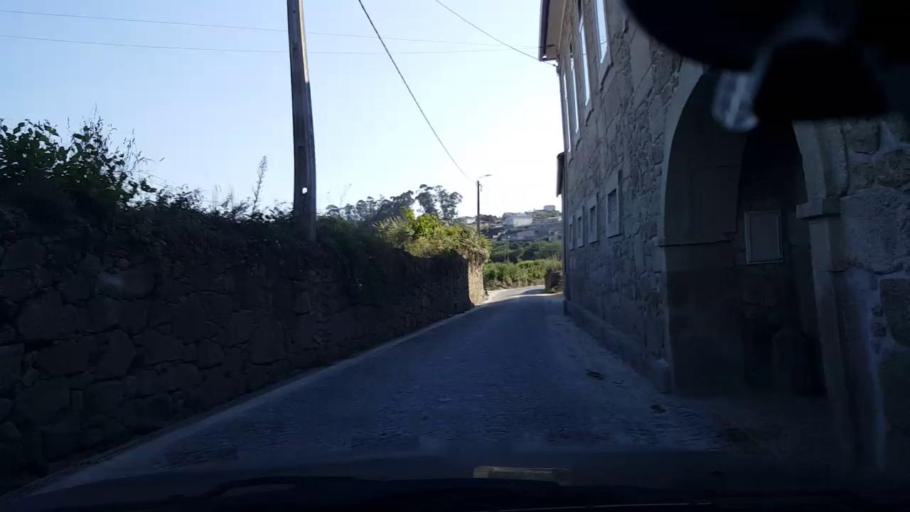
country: PT
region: Porto
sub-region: Vila do Conde
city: Arvore
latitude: 41.3595
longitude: -8.7211
